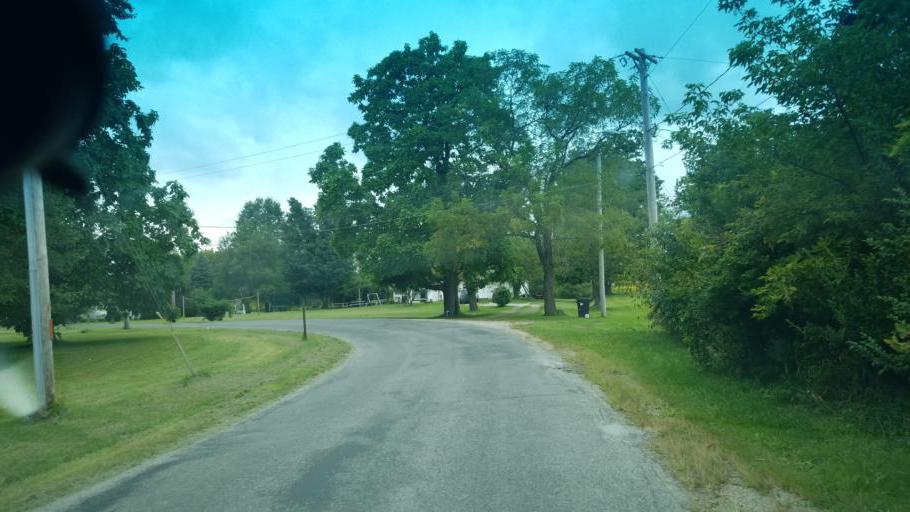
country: US
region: Ohio
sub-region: Huron County
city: Plymouth
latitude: 40.9717
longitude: -82.5960
